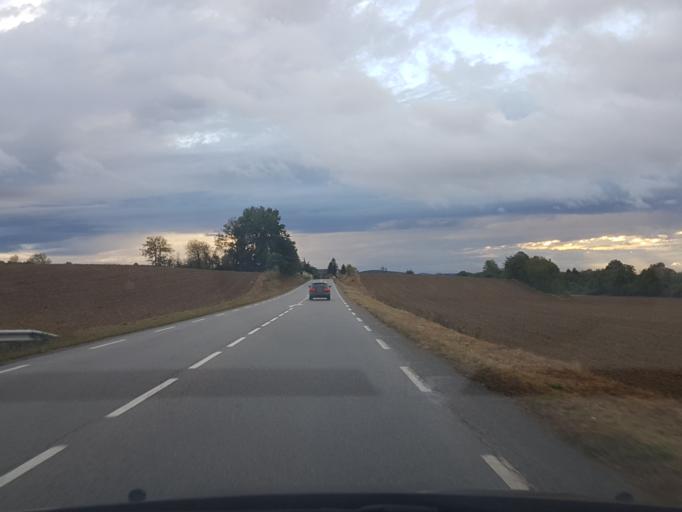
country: FR
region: Midi-Pyrenees
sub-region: Departement de l'Ariege
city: Mirepoix
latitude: 43.0767
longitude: 1.8322
